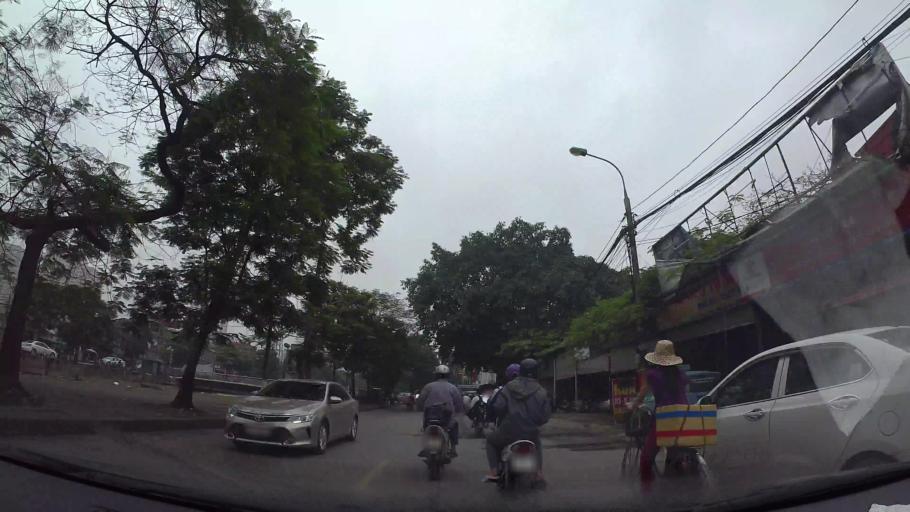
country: VN
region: Ha Noi
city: Hai BaTrung
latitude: 20.9917
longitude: 105.8625
